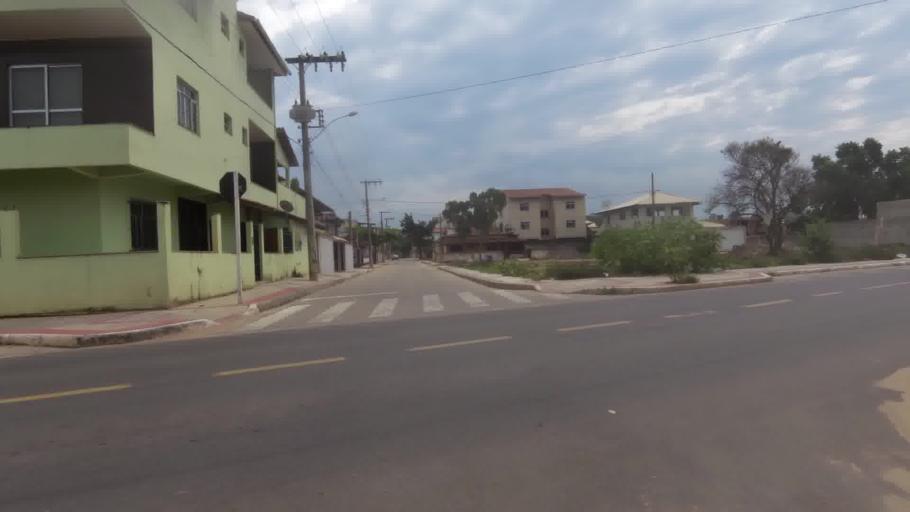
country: BR
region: Espirito Santo
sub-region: Piuma
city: Piuma
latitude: -20.8453
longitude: -40.7454
